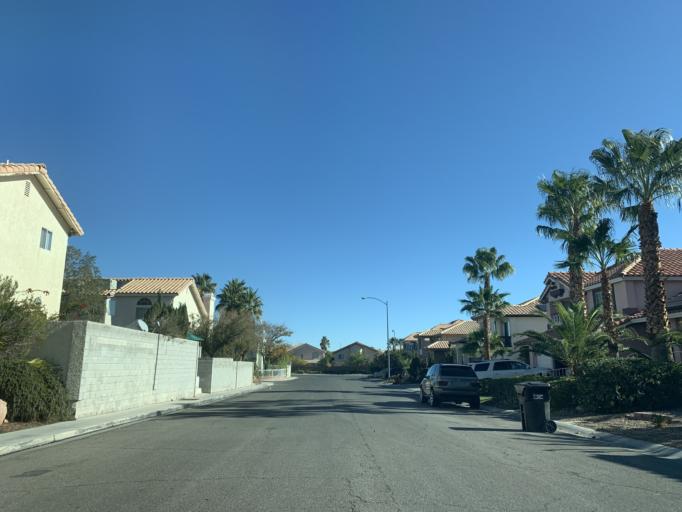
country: US
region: Nevada
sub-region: Clark County
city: Summerlin South
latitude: 36.1208
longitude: -115.2893
